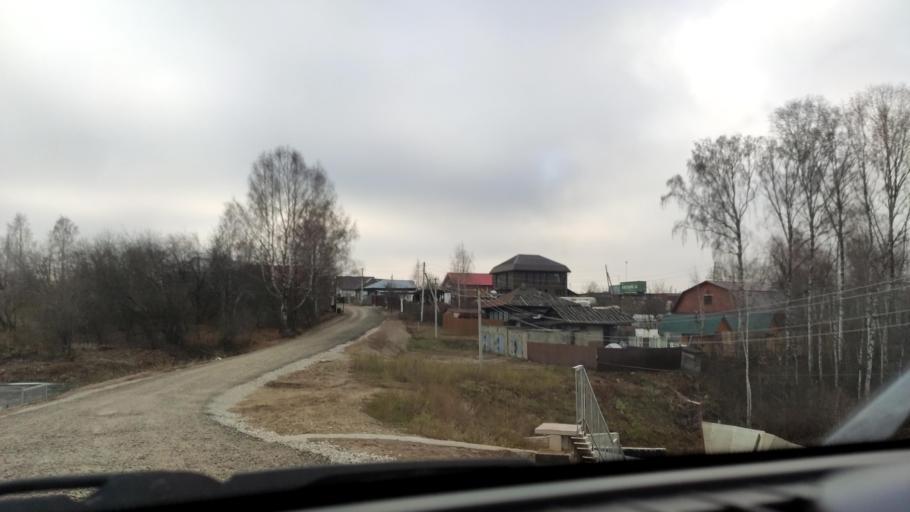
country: RU
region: Perm
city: Kondratovo
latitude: 57.9583
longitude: 56.1745
